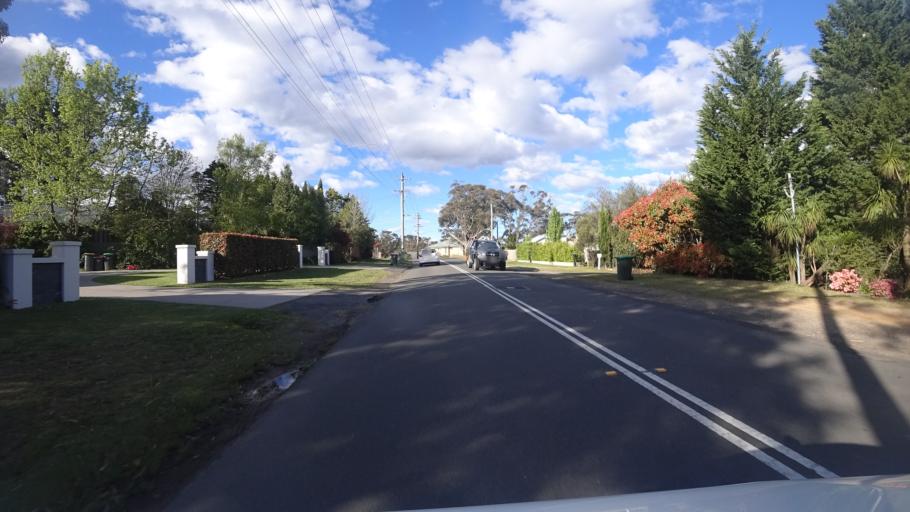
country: AU
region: New South Wales
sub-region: Blue Mountains Municipality
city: Katoomba
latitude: -33.7161
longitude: 150.2967
